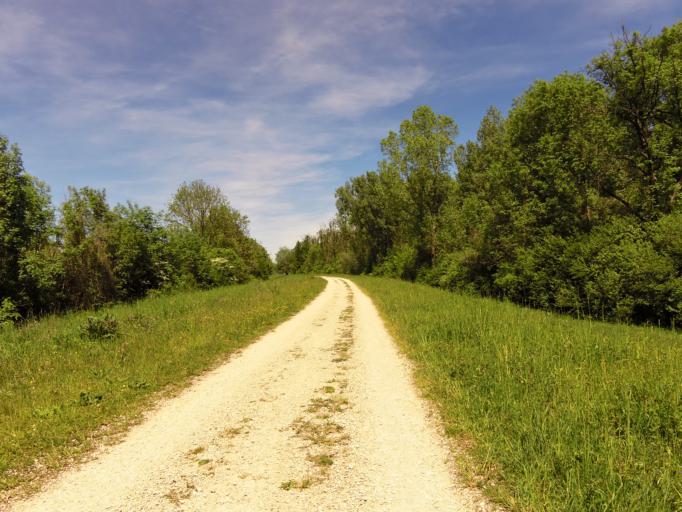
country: DE
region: Bavaria
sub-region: Upper Bavaria
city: Freising
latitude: 48.3827
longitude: 11.7387
